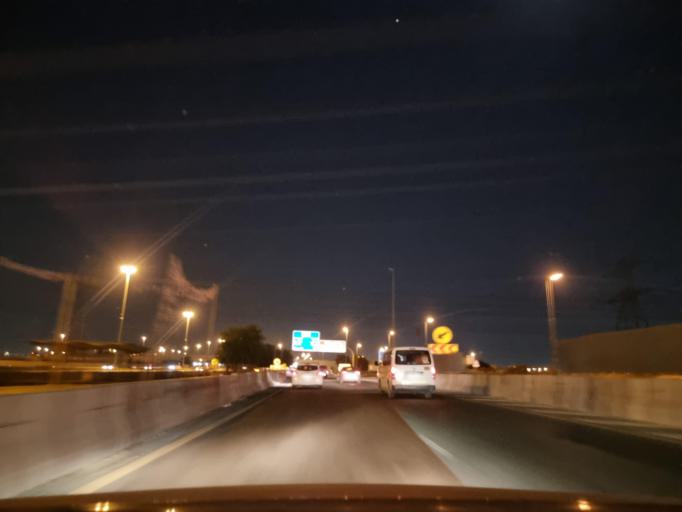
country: AE
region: Ash Shariqah
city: Sharjah
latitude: 25.1819
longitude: 55.3843
